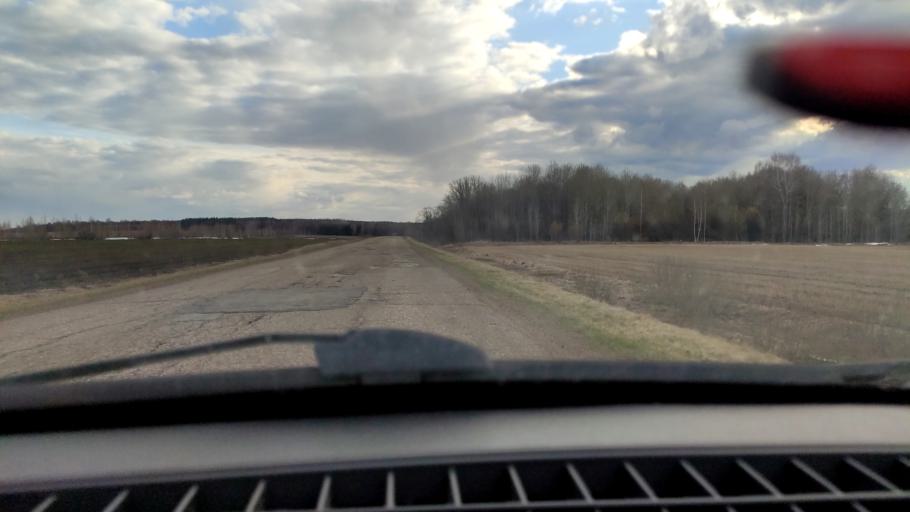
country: RU
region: Bashkortostan
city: Karmaskaly
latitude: 54.3247
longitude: 55.9867
